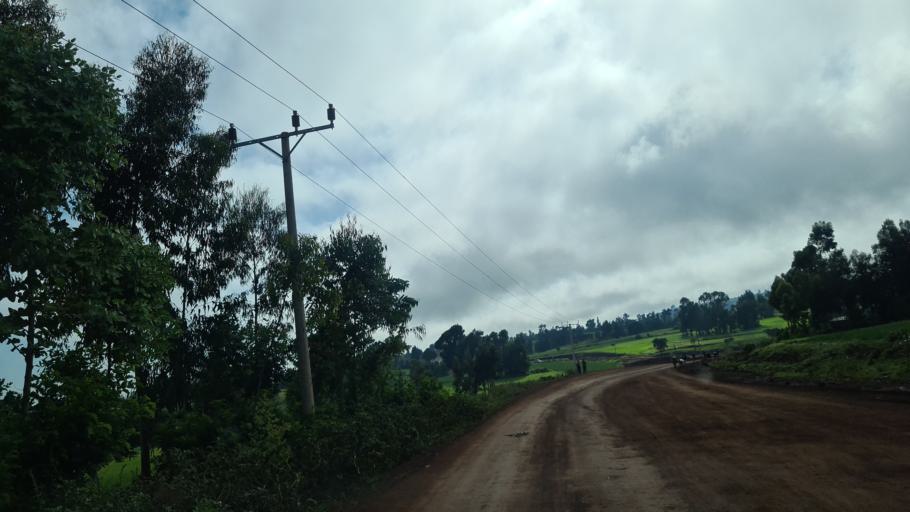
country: ET
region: Oromiya
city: Huruta
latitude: 8.1251
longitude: 39.3724
